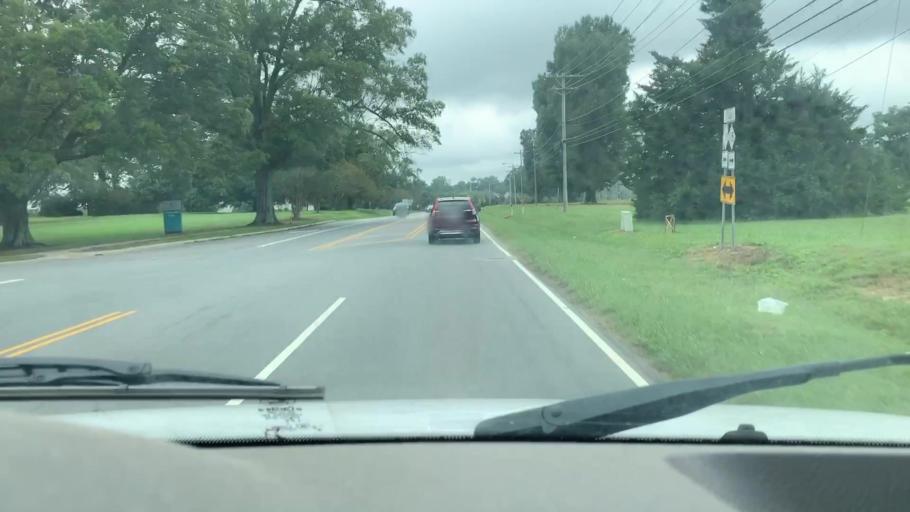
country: US
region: North Carolina
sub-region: Mecklenburg County
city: Huntersville
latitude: 35.3959
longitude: -80.8366
